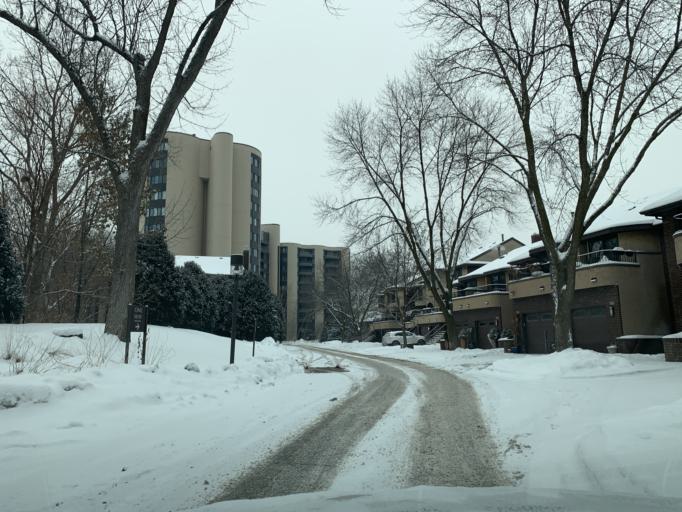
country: US
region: Minnesota
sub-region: Hennepin County
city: Saint Louis Park
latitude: 44.9509
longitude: -93.3186
